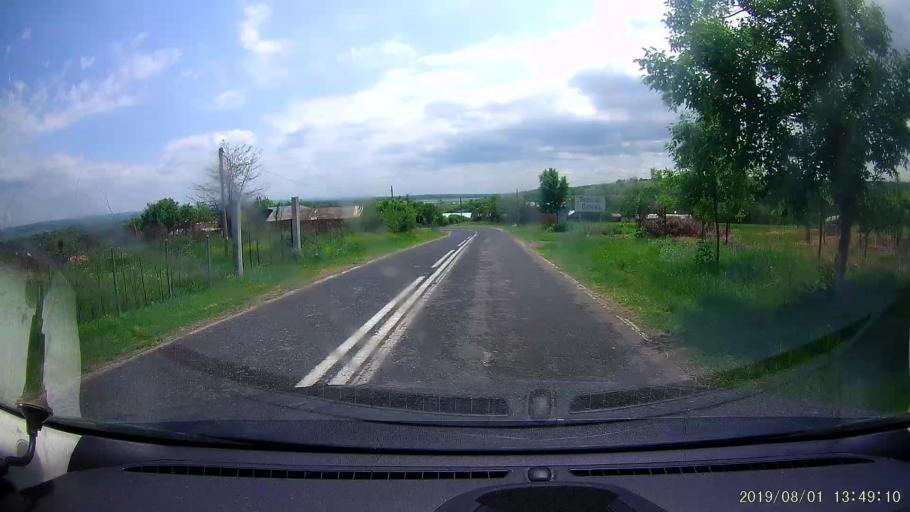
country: RO
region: Galati
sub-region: Comuna Oancea
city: Oancea
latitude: 45.8983
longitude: 28.1091
